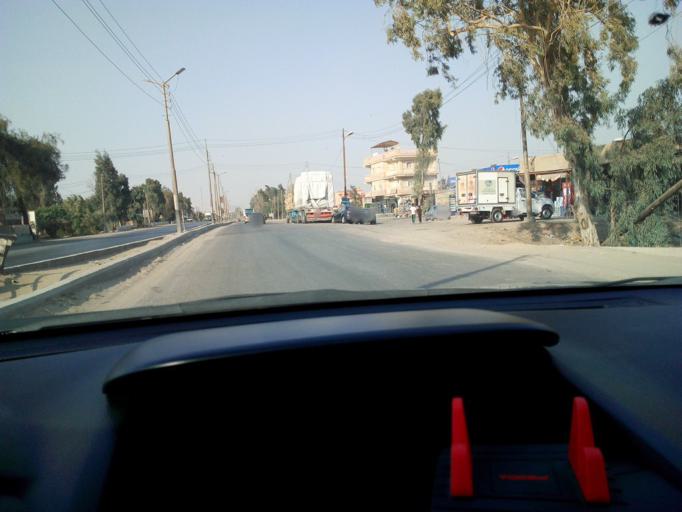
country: EG
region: Muhafazat al Fayyum
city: Tamiyah
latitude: 29.5512
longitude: 30.9288
